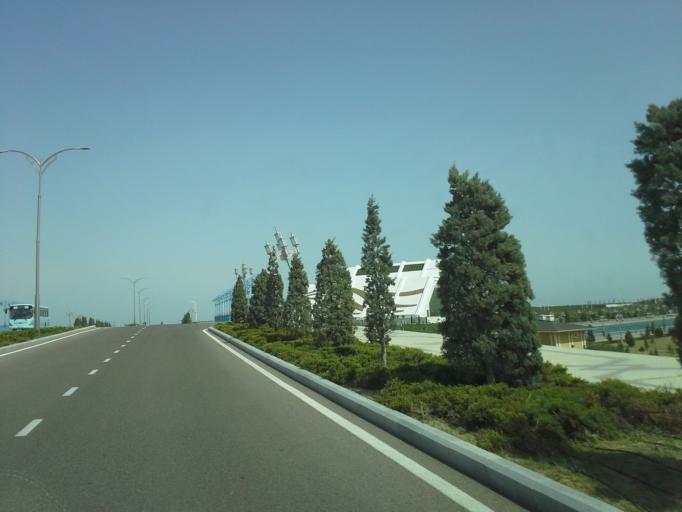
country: TM
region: Balkan
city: Turkmenbasy
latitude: 39.9476
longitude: 52.8807
